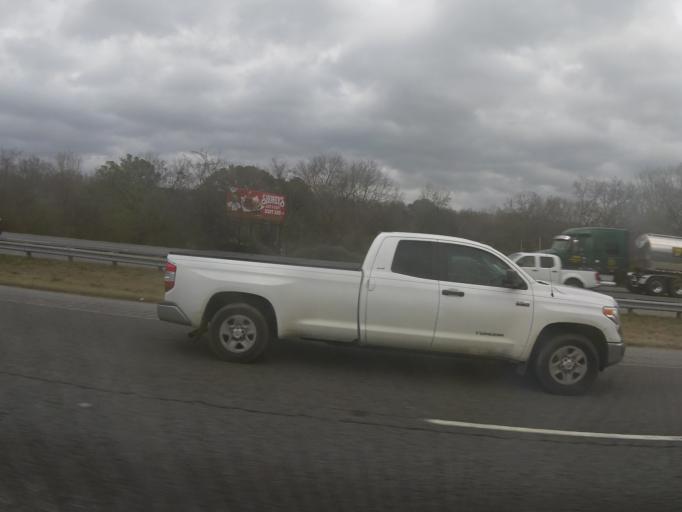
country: US
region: Georgia
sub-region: Whitfield County
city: Dalton
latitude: 34.6979
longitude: -85.0051
